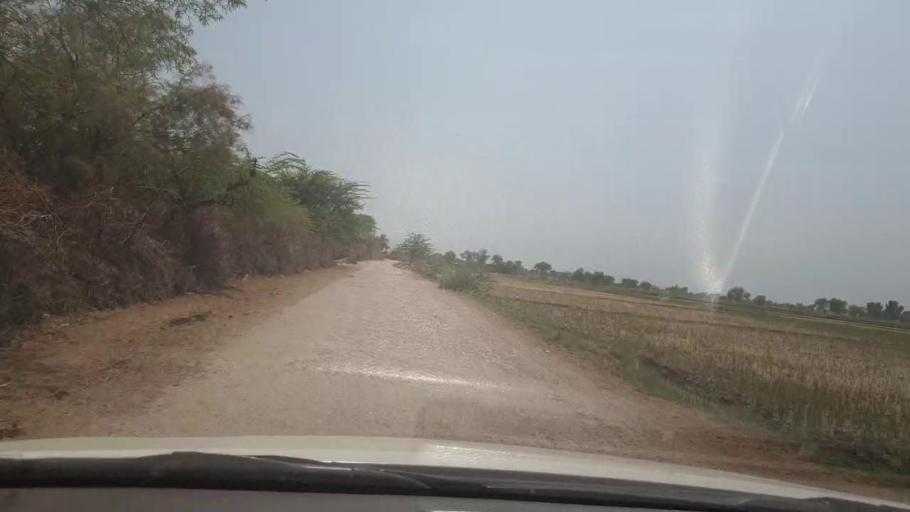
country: PK
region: Sindh
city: Shikarpur
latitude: 27.9989
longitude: 68.5895
